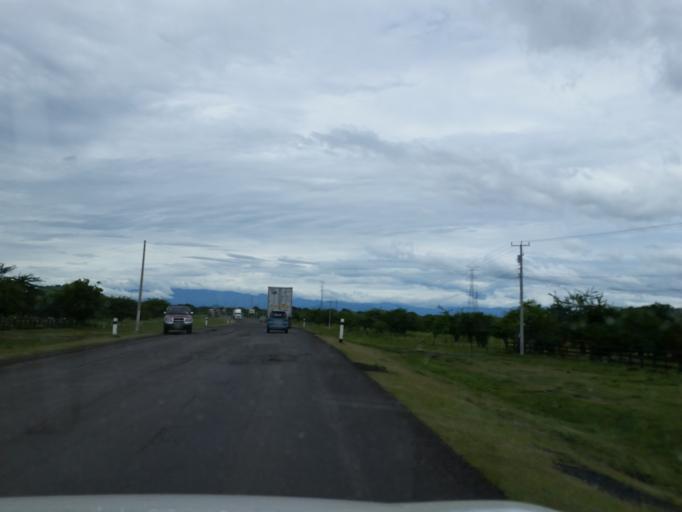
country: NI
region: Chinandega
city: Somotillo
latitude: 12.8832
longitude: -86.8504
